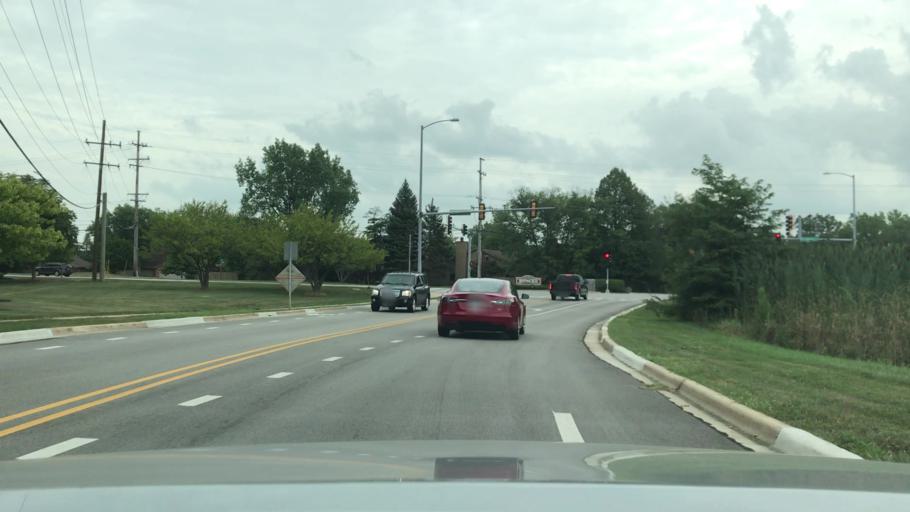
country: US
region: Illinois
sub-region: DuPage County
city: Darien
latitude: 41.7440
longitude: -87.9887
